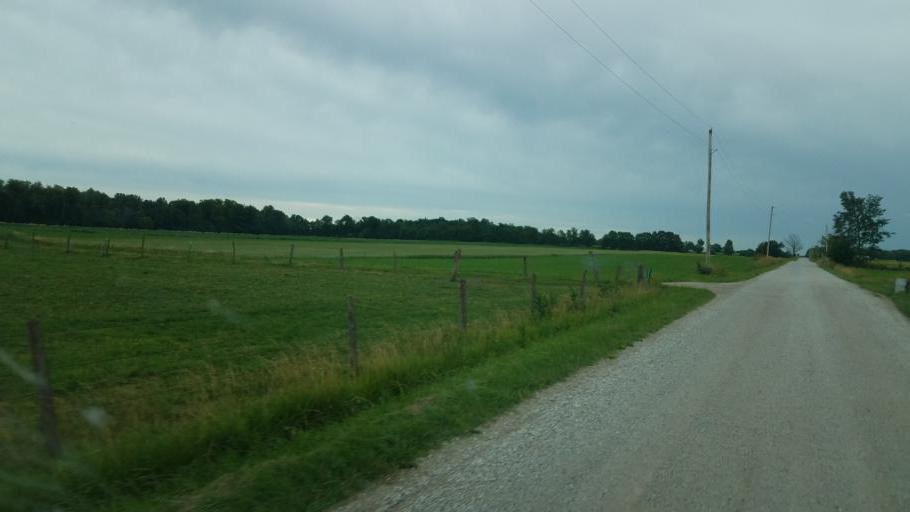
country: US
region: Ohio
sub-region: Huron County
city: Greenwich
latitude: 40.9436
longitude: -82.4313
